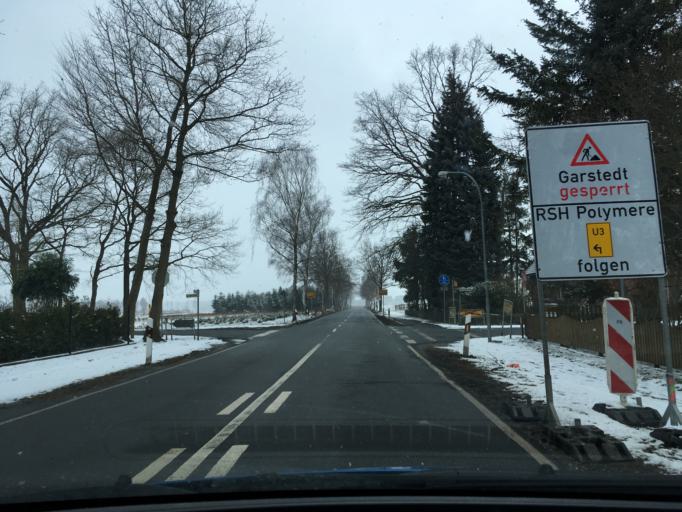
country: DE
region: Lower Saxony
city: Vierhofen
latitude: 53.2751
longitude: 10.2128
